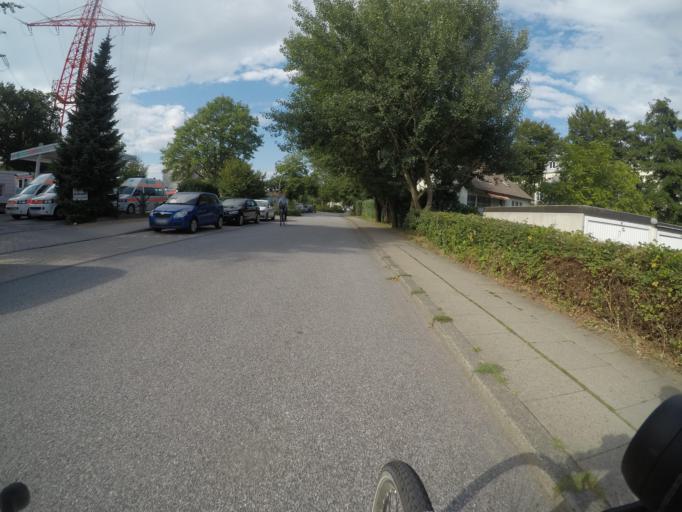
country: DE
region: Schleswig-Holstein
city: Glinde
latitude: 53.5077
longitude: 10.1846
